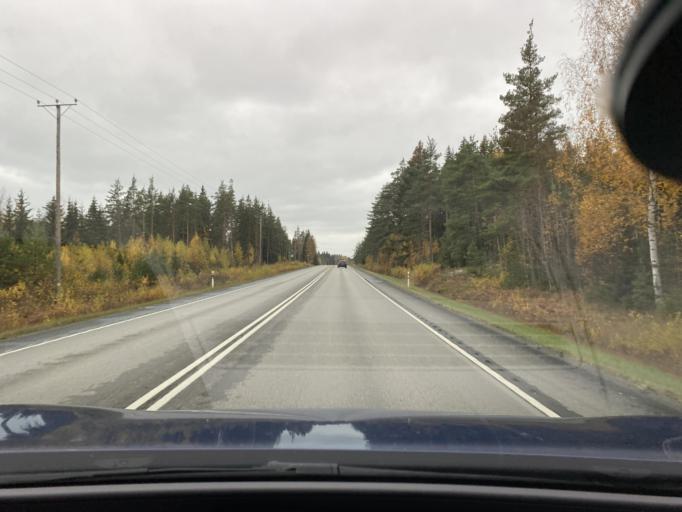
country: FI
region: Satakunta
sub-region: Rauma
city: Lappi
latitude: 61.1067
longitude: 21.9108
